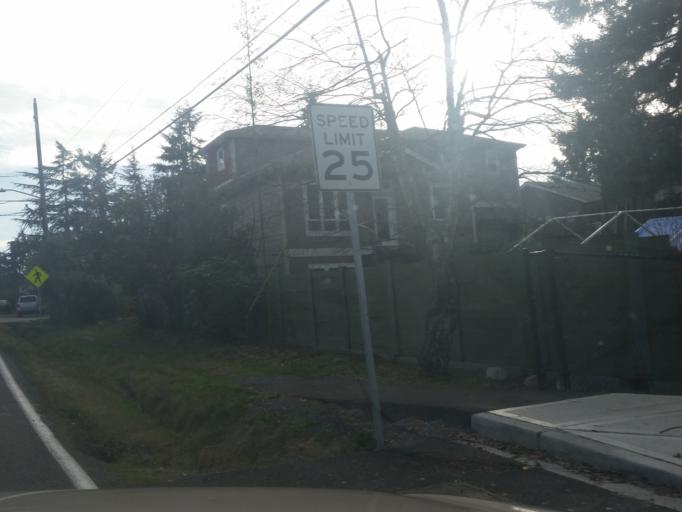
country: US
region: Washington
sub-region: King County
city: Shoreline
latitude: 47.7705
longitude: -122.3299
